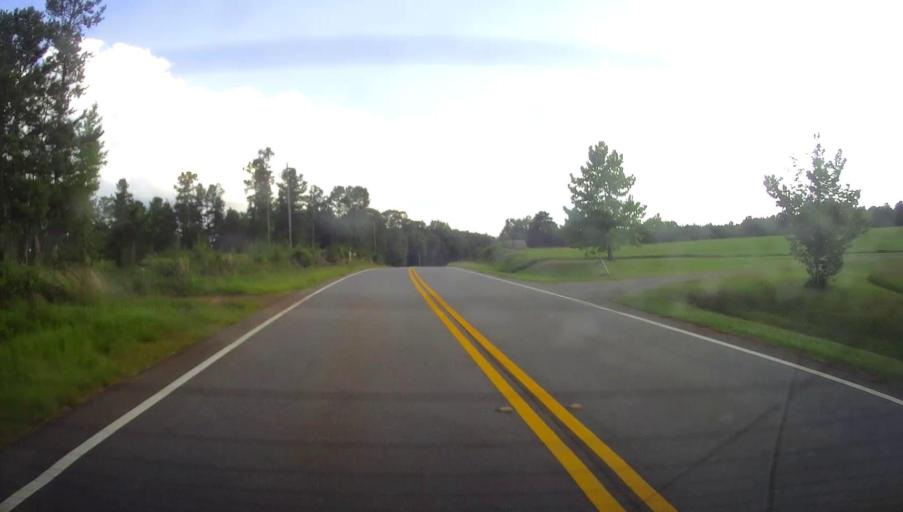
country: US
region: Georgia
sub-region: Monroe County
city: Forsyth
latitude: 32.9349
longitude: -83.9605
